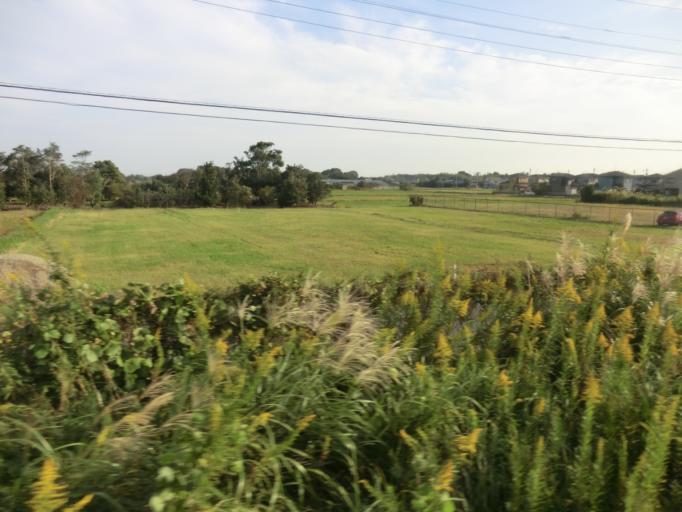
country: JP
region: Chiba
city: Yokaichiba
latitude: 35.6845
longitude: 140.5205
